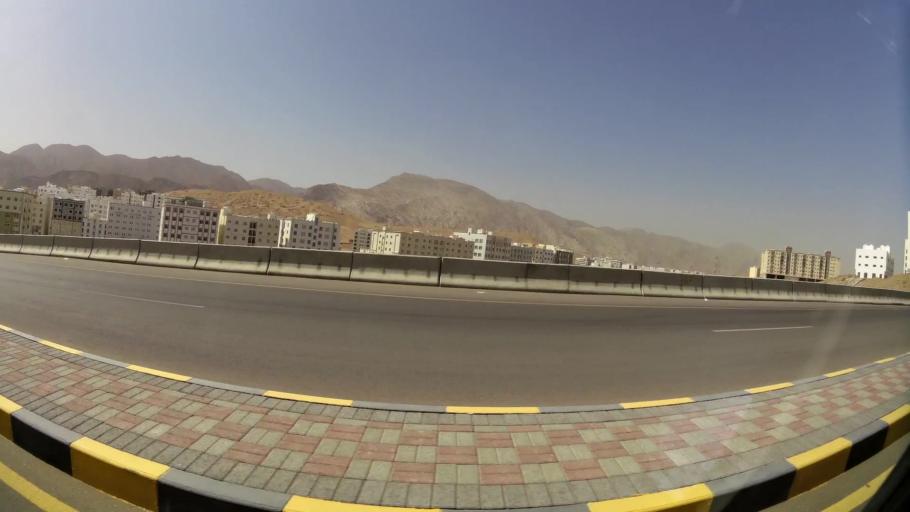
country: OM
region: Muhafazat Masqat
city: Bawshar
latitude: 23.5780
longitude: 58.4162
